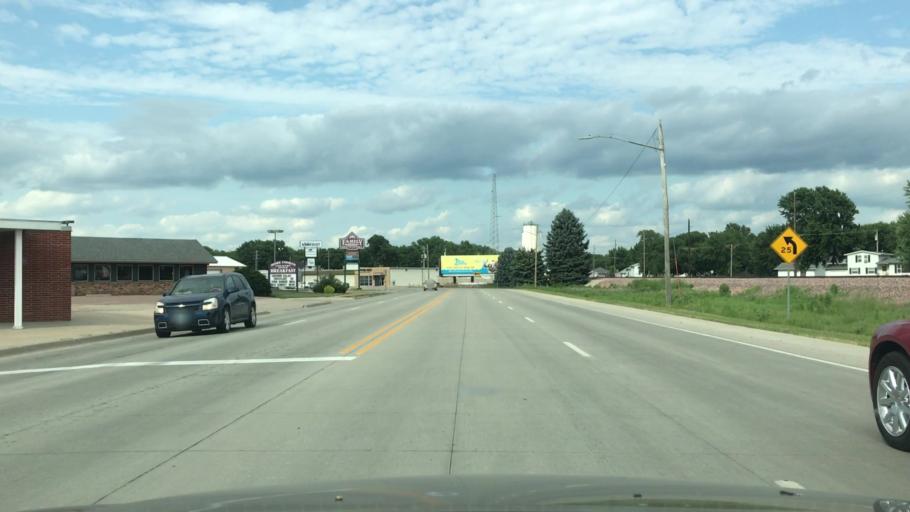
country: US
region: Iowa
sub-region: Plymouth County
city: Le Mars
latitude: 42.7861
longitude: -96.1752
